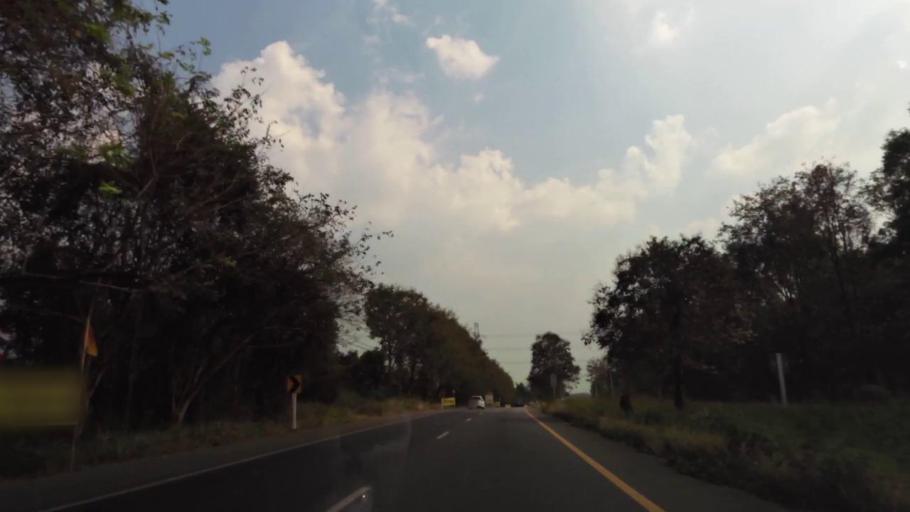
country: TH
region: Chon Buri
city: Nong Yai
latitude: 13.1526
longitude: 101.3254
